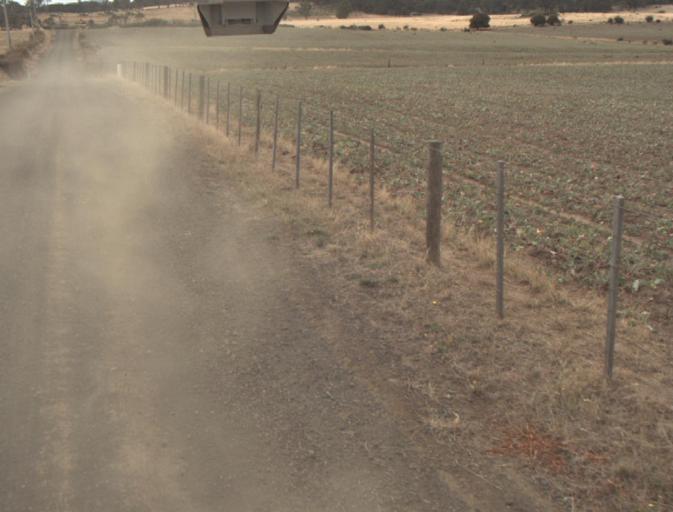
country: AU
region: Tasmania
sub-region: Northern Midlands
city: Evandale
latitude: -41.5180
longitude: 147.2905
